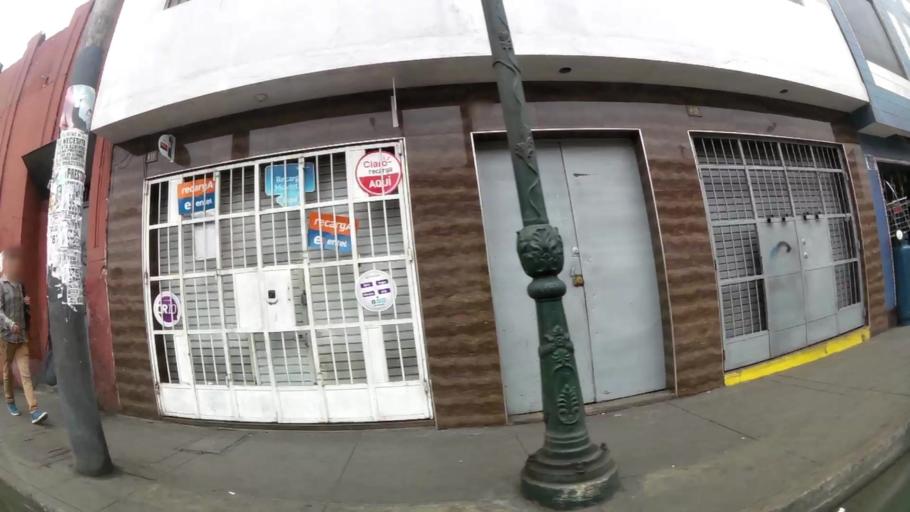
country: PE
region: Lima
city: Lima
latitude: -12.0447
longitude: -77.0406
